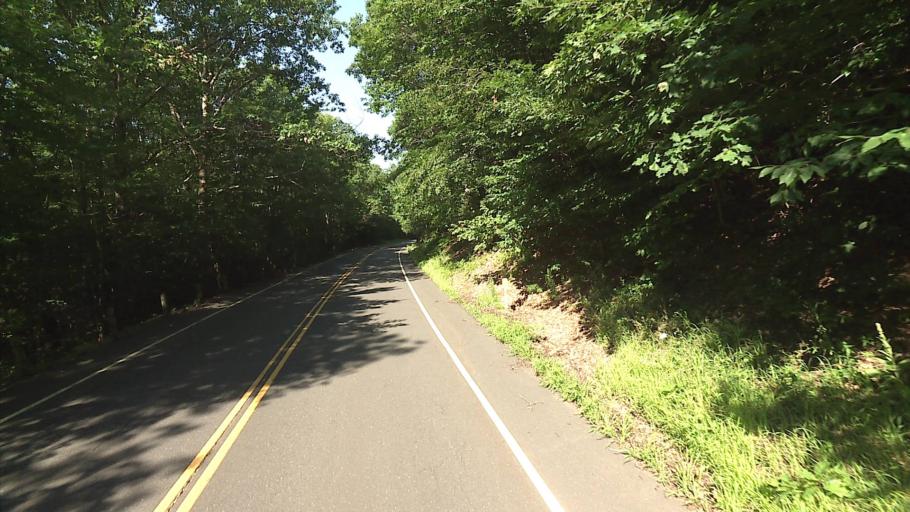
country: US
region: Massachusetts
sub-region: Hampden County
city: Granville
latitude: 42.0156
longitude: -72.9226
